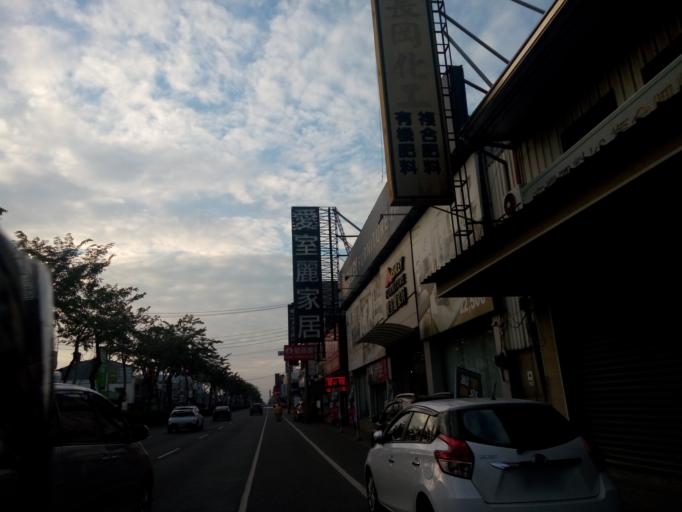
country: TW
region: Taiwan
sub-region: Chiayi
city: Jiayi Shi
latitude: 23.4865
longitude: 120.4164
